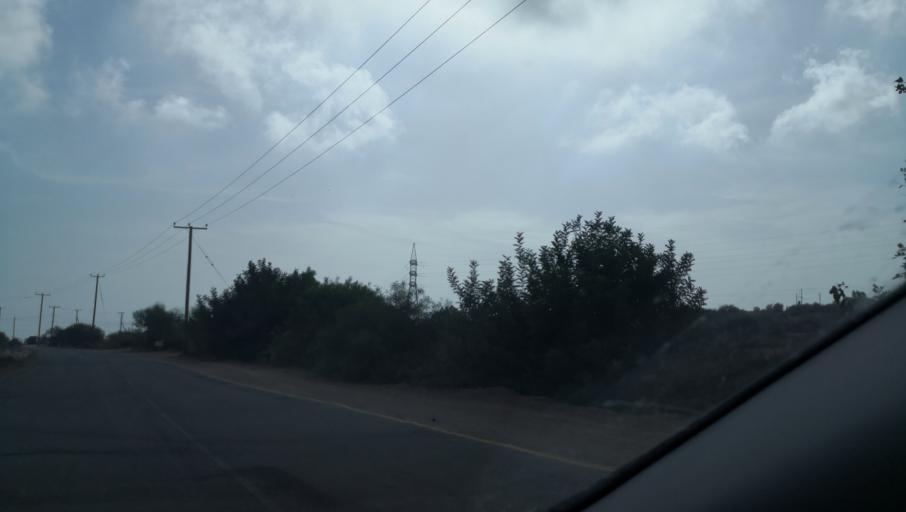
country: CY
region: Ammochostos
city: Protaras
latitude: 35.0148
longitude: 34.0285
